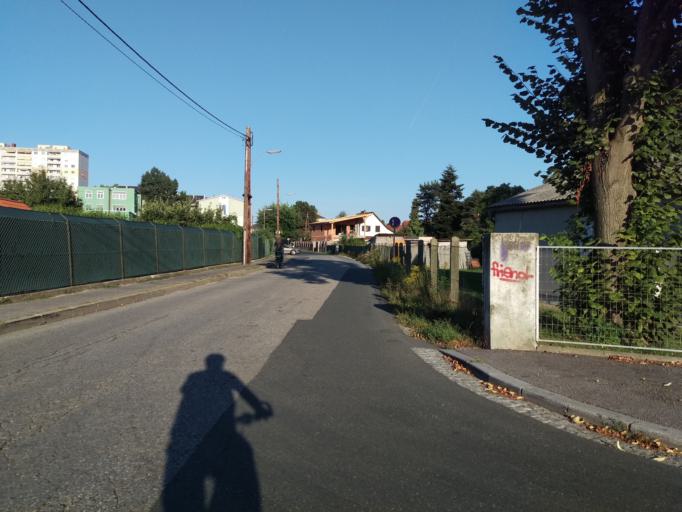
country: AT
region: Styria
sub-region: Graz Stadt
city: Wetzelsdorf
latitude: 47.0542
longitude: 15.4220
